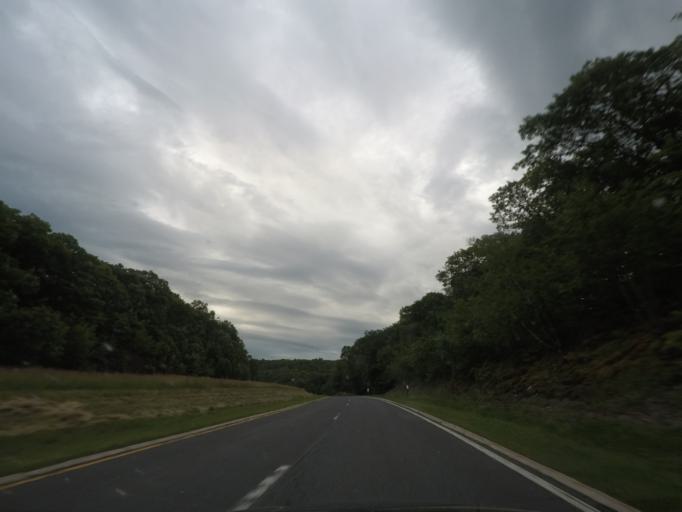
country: US
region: New York
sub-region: Columbia County
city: Philmont
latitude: 42.1837
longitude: -73.6519
